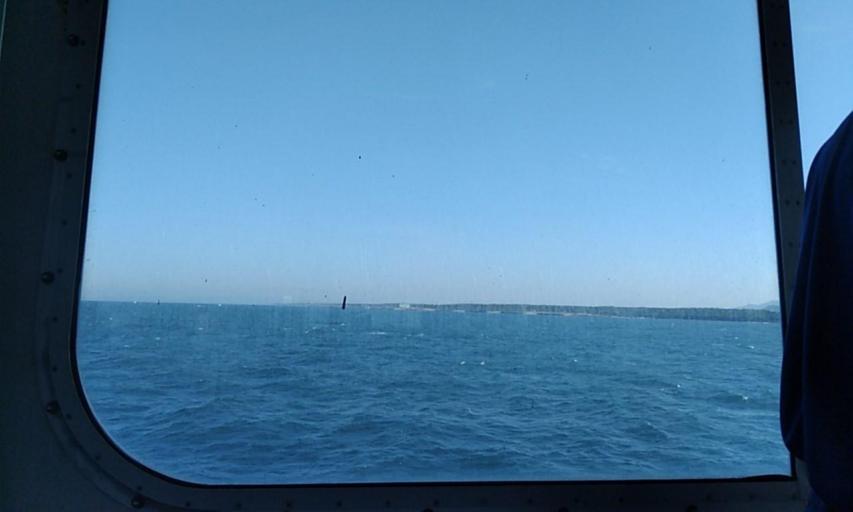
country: JP
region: Aichi
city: Toyohama
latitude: 34.5910
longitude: 137.0206
